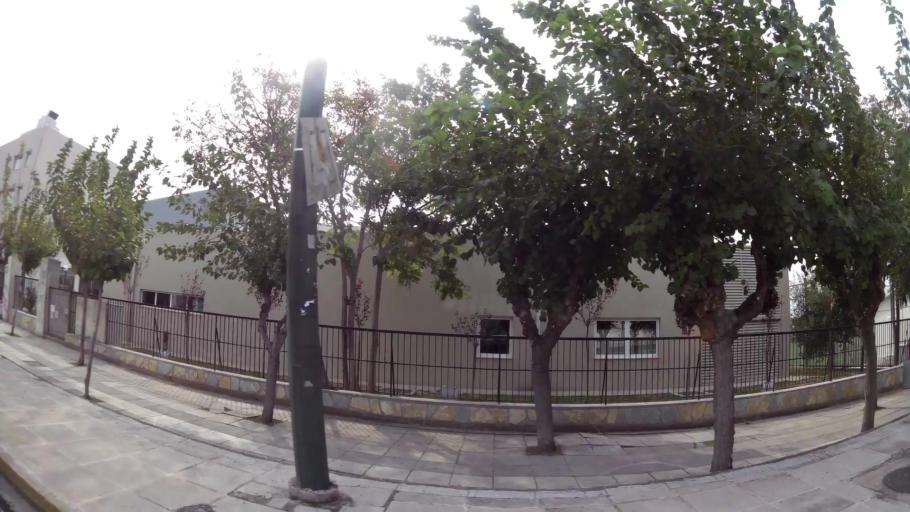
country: GR
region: Attica
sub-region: Nomarchia Athinas
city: Athens
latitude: 37.9741
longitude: 23.7069
